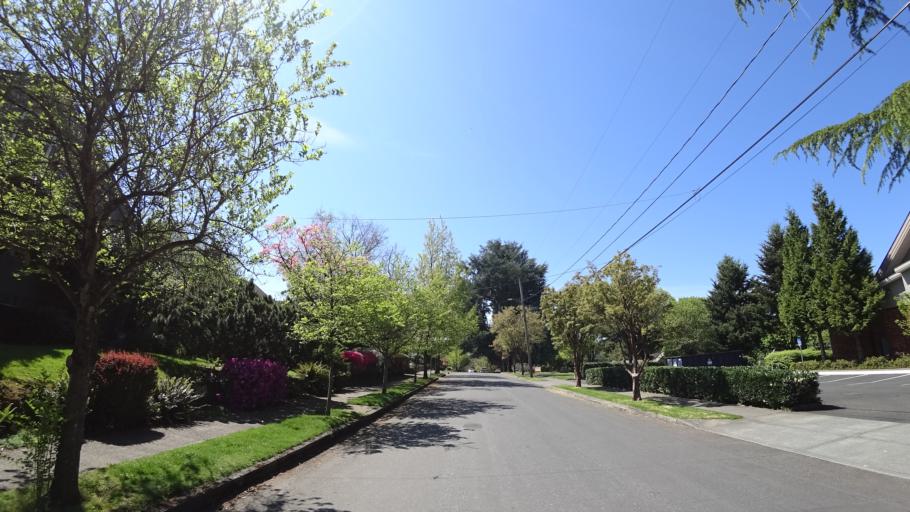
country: US
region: Oregon
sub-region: Clackamas County
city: Milwaukie
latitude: 45.4685
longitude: -122.6228
